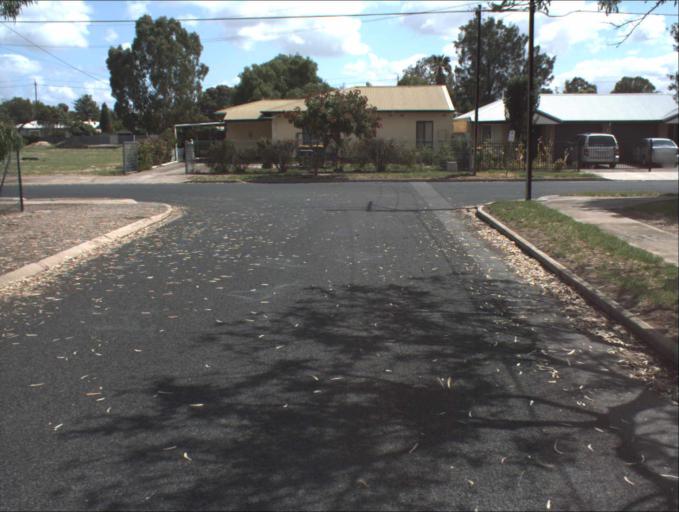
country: AU
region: South Australia
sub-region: Port Adelaide Enfield
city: Enfield
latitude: -34.8509
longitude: 138.5945
